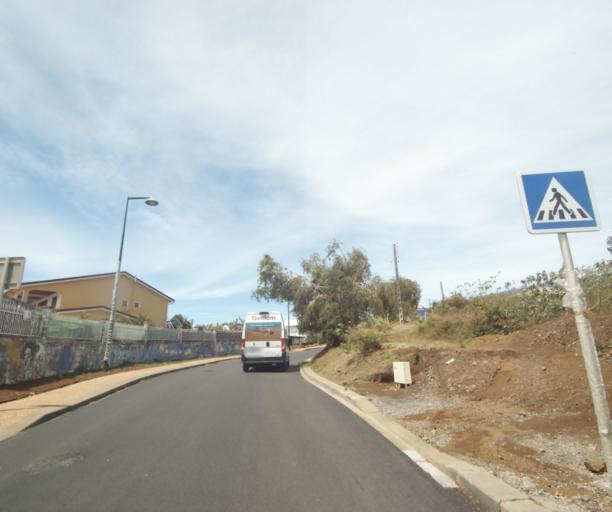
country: RE
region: Reunion
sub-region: Reunion
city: Saint-Paul
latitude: -21.0403
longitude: 55.3026
